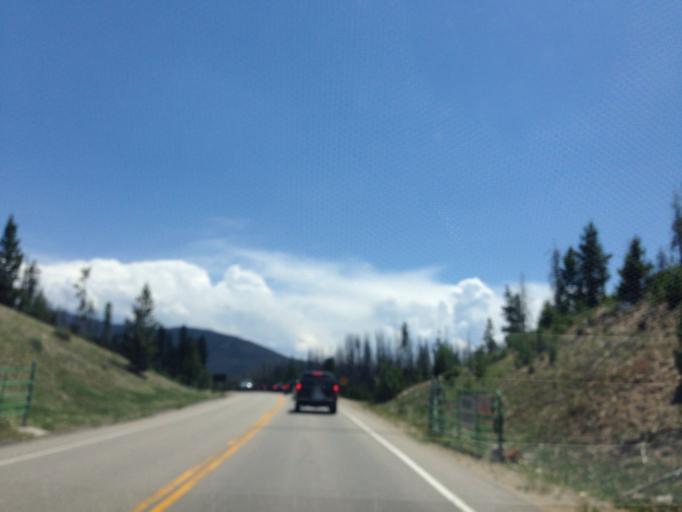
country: US
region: Colorado
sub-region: Grand County
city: Granby
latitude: 40.2683
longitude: -105.8343
